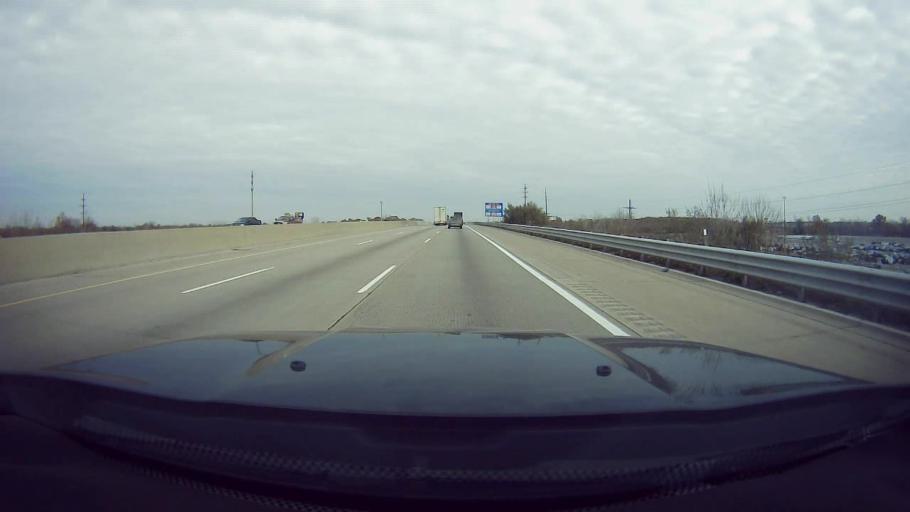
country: US
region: Michigan
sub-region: Wayne County
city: Woodhaven
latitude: 42.1213
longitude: -83.2415
